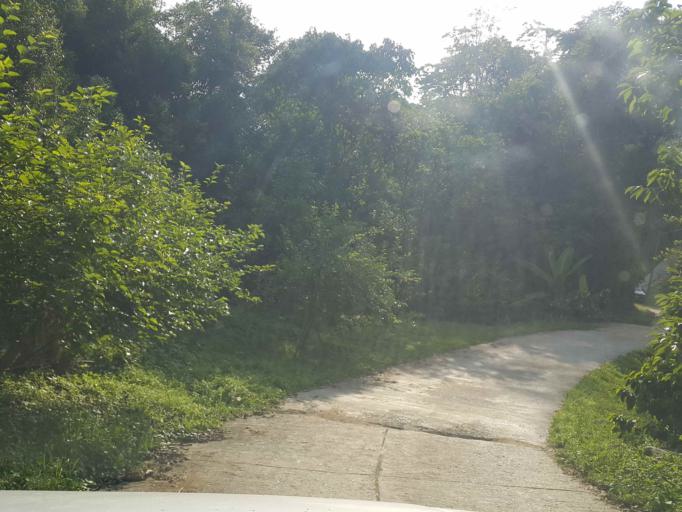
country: TH
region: Chiang Mai
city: Mae On
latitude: 18.9243
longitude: 99.3587
